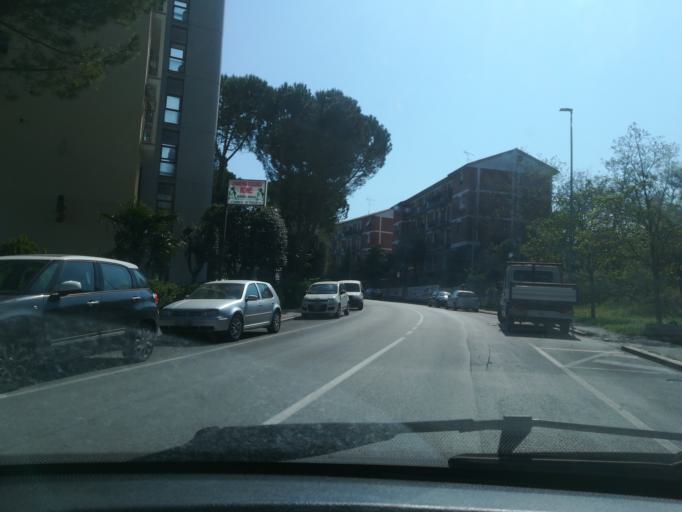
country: IT
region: The Marches
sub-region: Provincia di Macerata
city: Macerata
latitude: 43.2837
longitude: 13.4302
